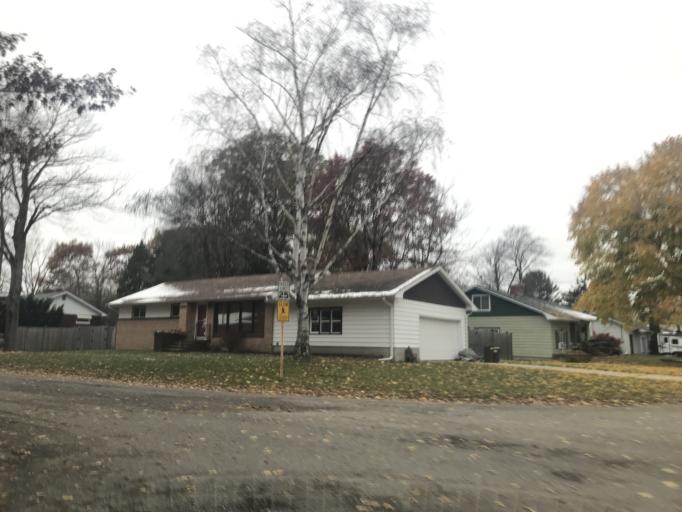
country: US
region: Wisconsin
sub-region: Marinette County
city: Marinette
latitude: 45.0975
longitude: -87.6557
